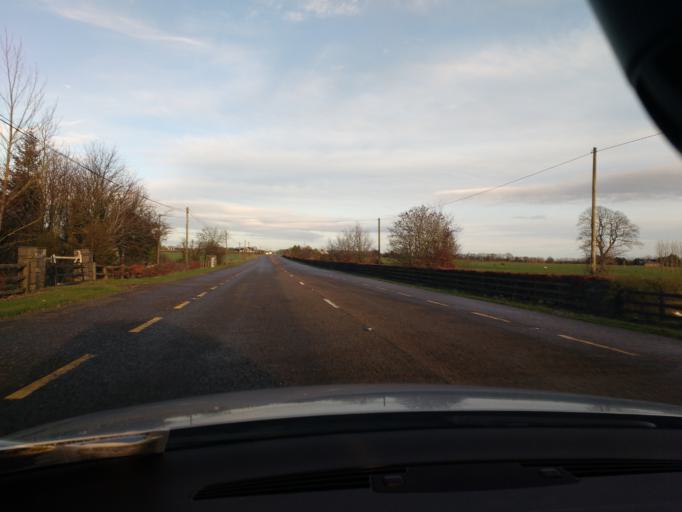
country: IE
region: Munster
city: Thurles
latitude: 52.6633
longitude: -7.6953
